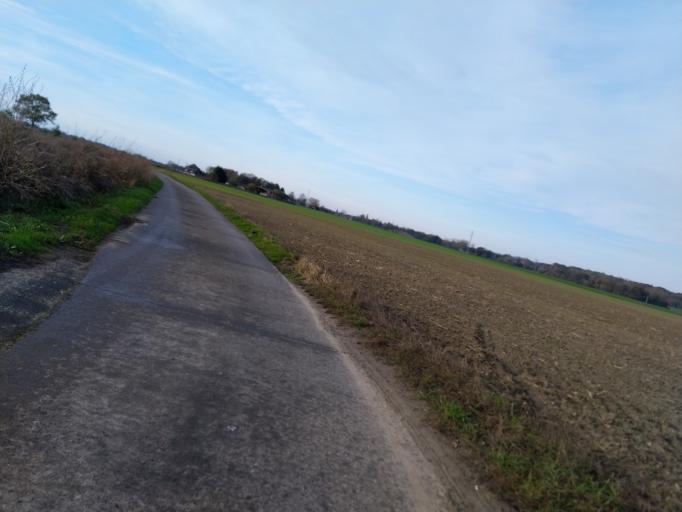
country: BE
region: Wallonia
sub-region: Province du Hainaut
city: Saint-Ghislain
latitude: 50.5111
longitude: 3.8158
